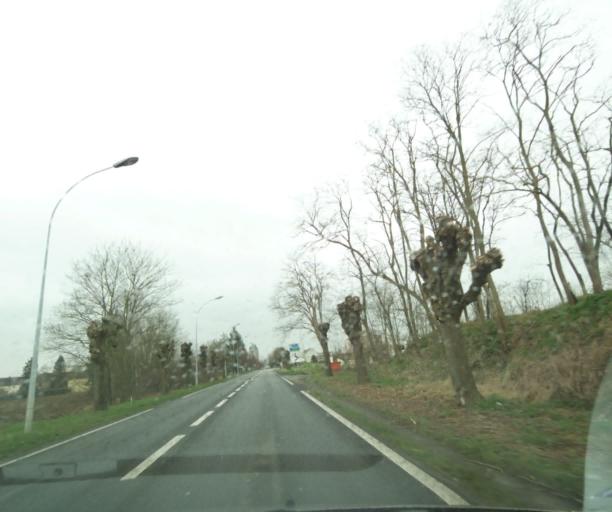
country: FR
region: Picardie
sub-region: Departement de l'Oise
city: Noyon
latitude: 49.5907
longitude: 3.0031
